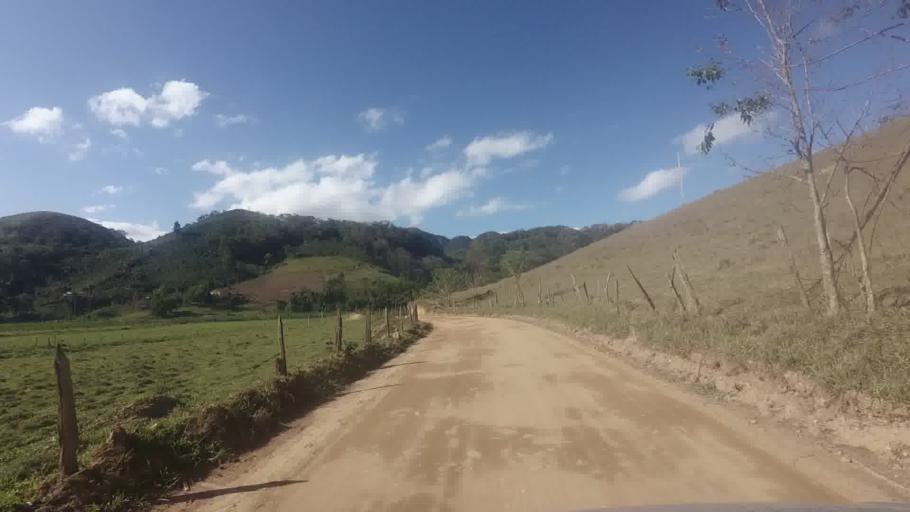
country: BR
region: Espirito Santo
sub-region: Sao Jose Do Calcado
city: Sao Jose do Calcado
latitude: -21.0224
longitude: -41.5685
